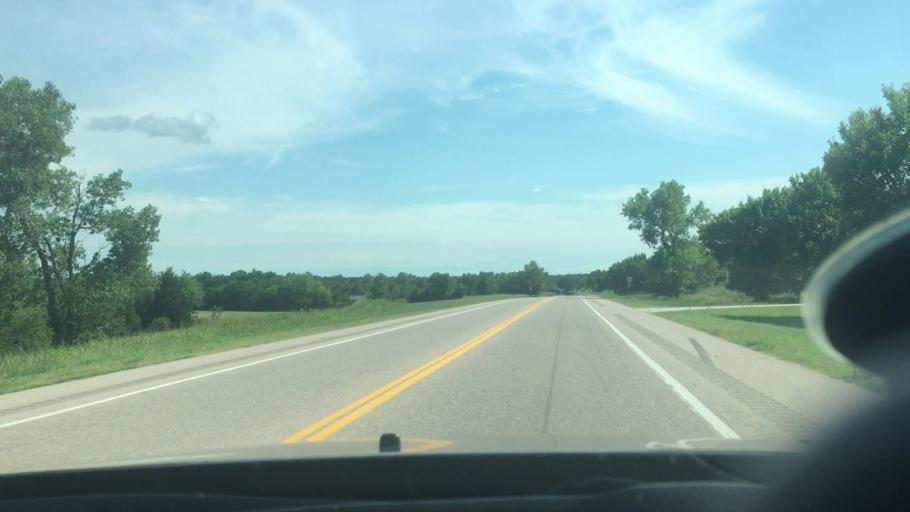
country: US
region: Oklahoma
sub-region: Seminole County
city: Seminole
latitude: 35.1555
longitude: -96.6747
